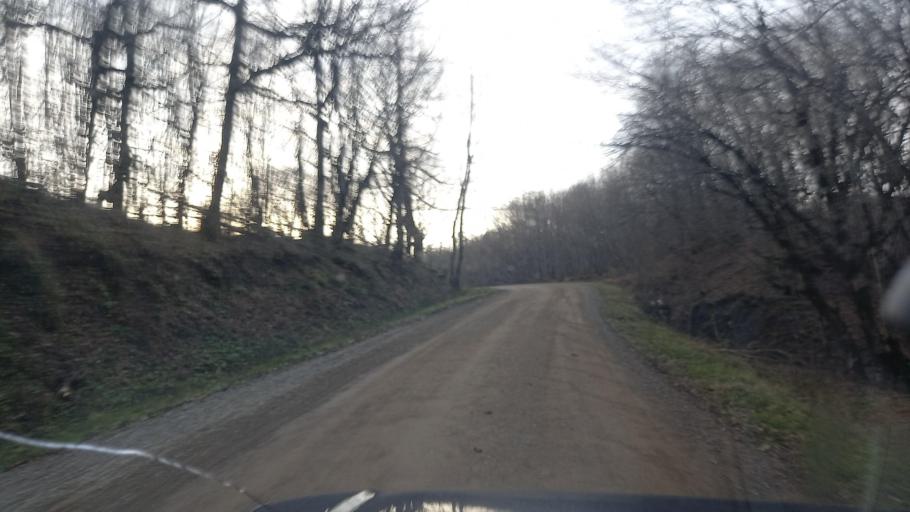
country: RU
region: Krasnodarskiy
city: Khadyzhensk
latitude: 44.3369
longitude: 39.2792
